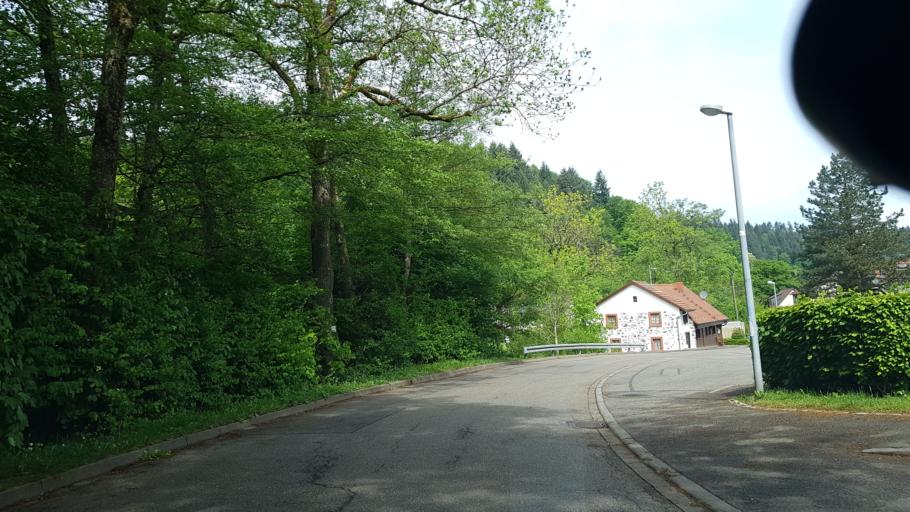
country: DE
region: Baden-Wuerttemberg
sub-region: Freiburg Region
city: Kirchzarten
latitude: 47.9625
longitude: 7.9094
